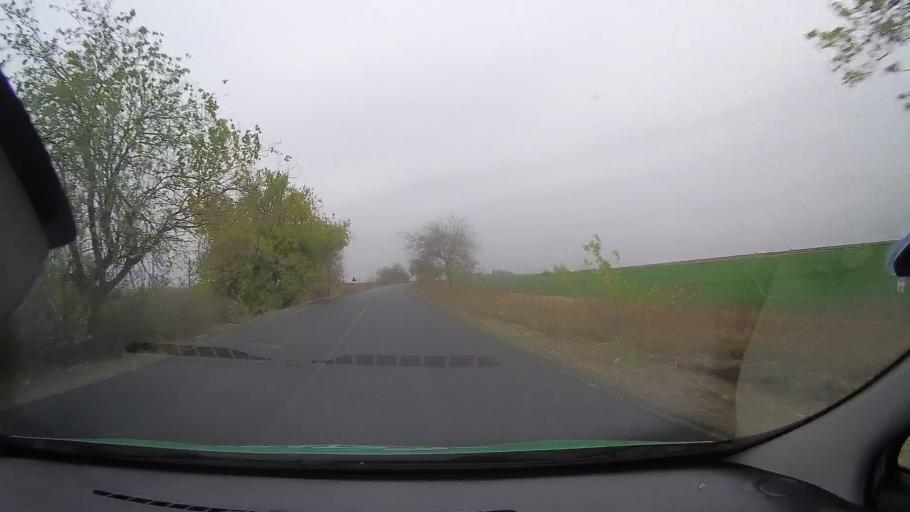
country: RO
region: Ialomita
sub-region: Comuna Valea Ciorii
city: Valea Ciorii
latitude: 44.6968
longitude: 27.6007
